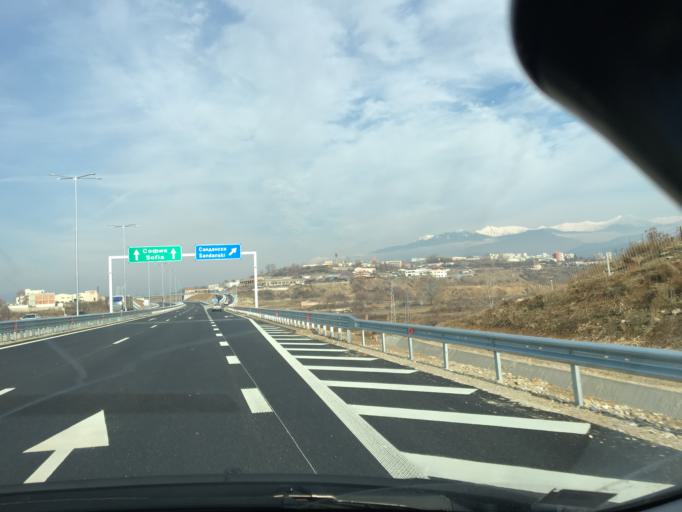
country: BG
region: Blagoevgrad
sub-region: Obshtina Sandanski
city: Sandanski
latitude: 41.5360
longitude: 23.2581
